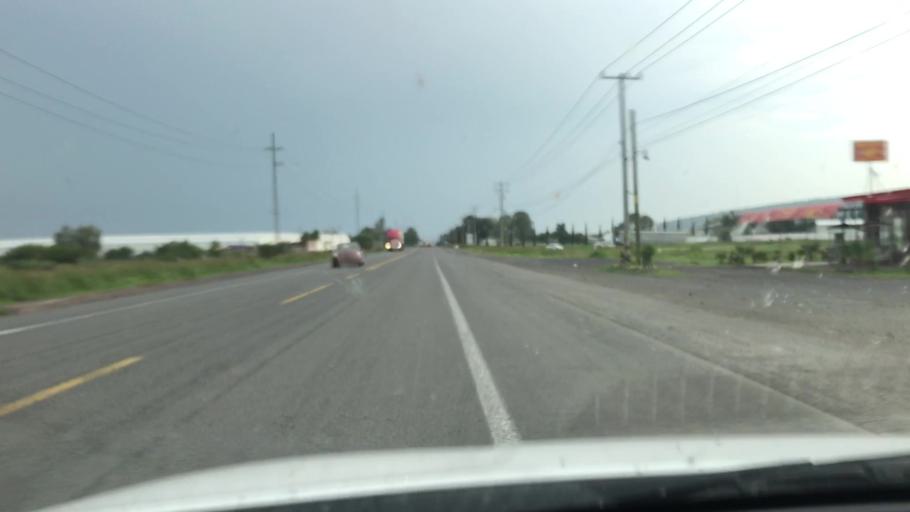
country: MX
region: Michoacan
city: Tanhuato de Guerrero
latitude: 20.2804
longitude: -102.3613
